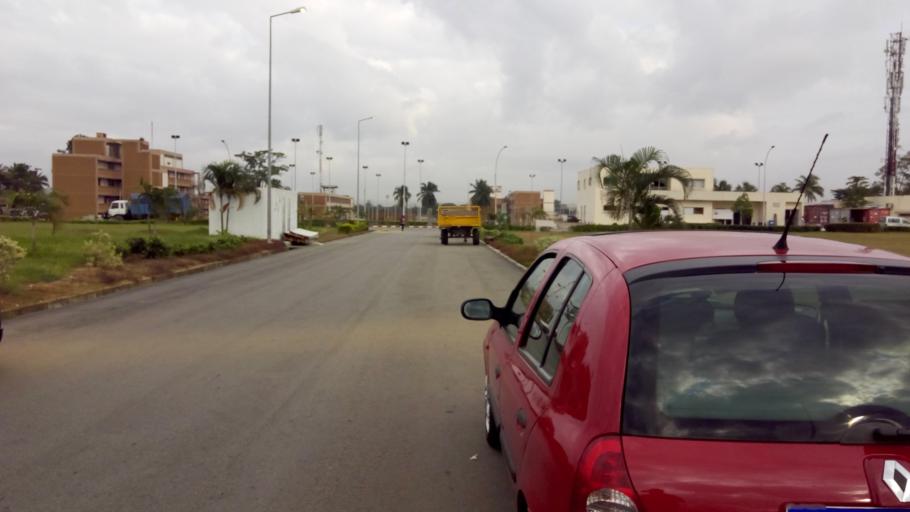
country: CI
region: Lagunes
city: Abidjan
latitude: 5.3420
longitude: -3.9871
